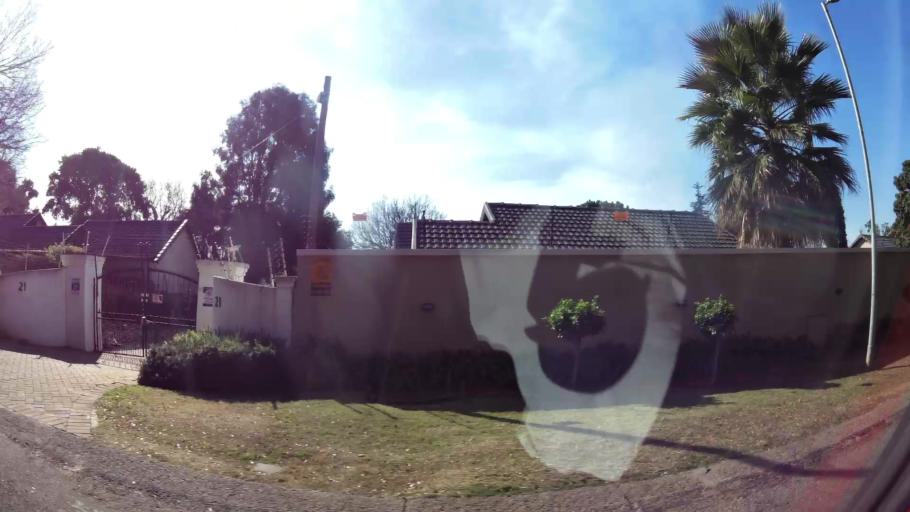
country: ZA
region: Gauteng
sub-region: City of Johannesburg Metropolitan Municipality
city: Roodepoort
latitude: -26.1079
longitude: 27.9536
